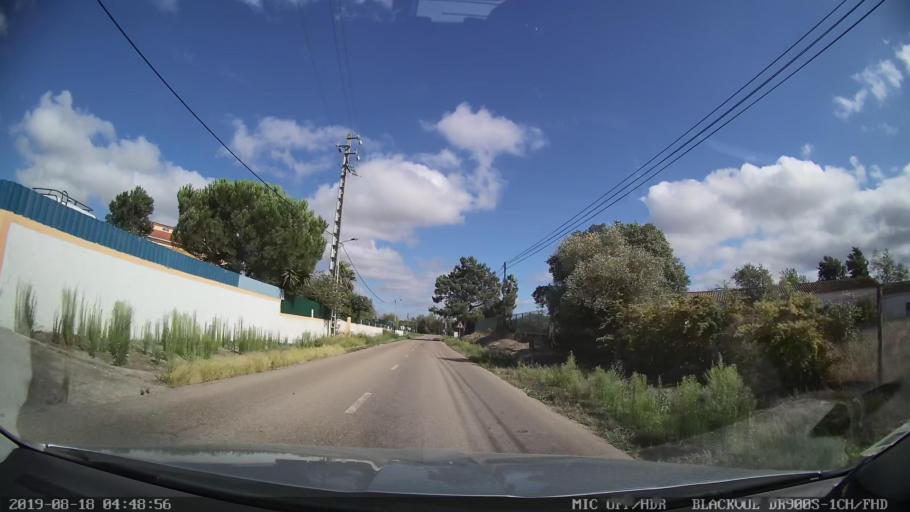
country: PT
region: Santarem
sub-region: Benavente
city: Benavente
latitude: 38.9410
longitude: -8.8005
